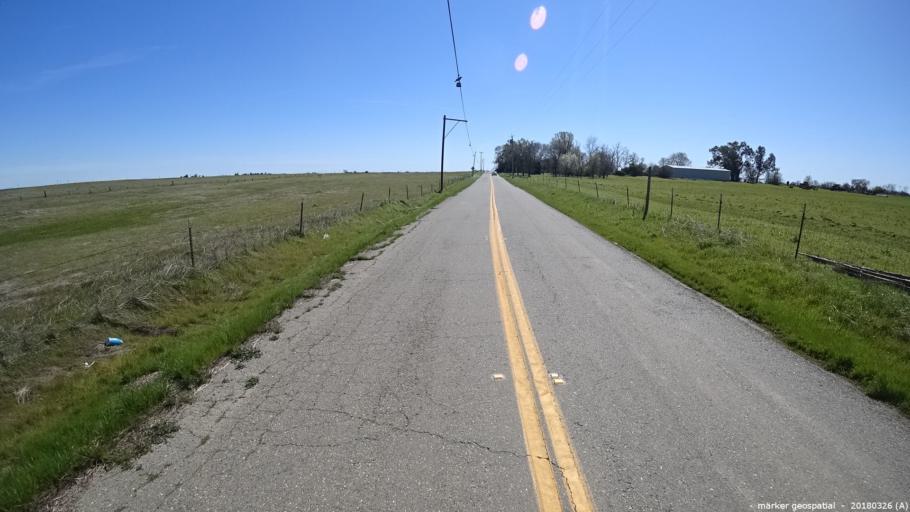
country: US
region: California
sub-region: Sacramento County
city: Wilton
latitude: 38.4818
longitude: -121.2607
